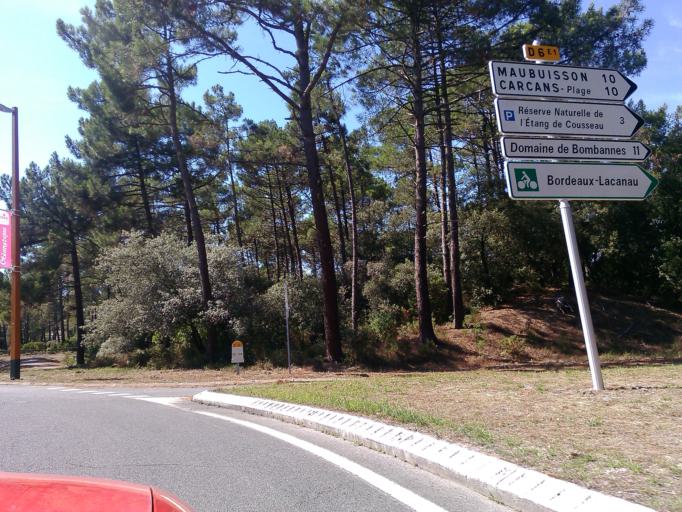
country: FR
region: Aquitaine
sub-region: Departement de la Gironde
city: Lacanau
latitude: 45.0063
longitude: -1.1758
